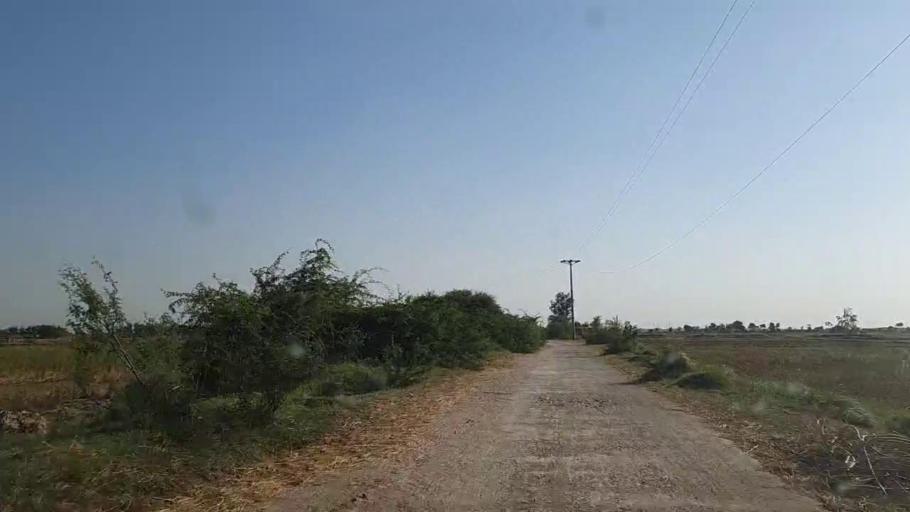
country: PK
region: Sindh
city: Thatta
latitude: 24.6357
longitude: 68.0763
